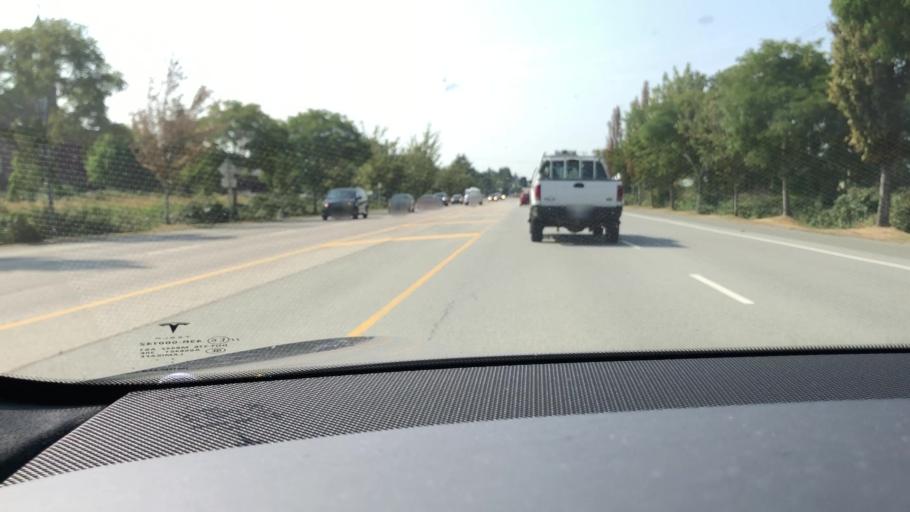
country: CA
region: British Columbia
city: Ladner
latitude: 49.0395
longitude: -123.0687
